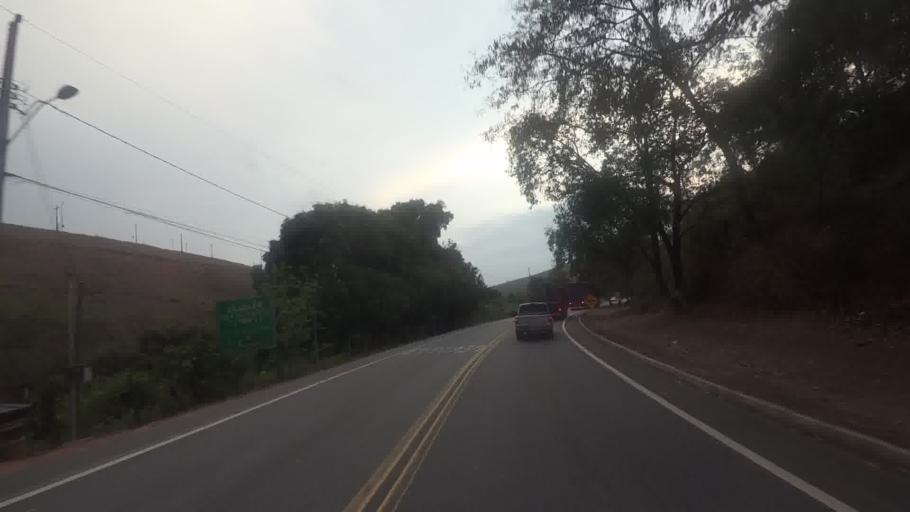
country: BR
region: Rio de Janeiro
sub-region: Carmo
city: Carmo
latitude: -21.8178
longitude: -42.5985
